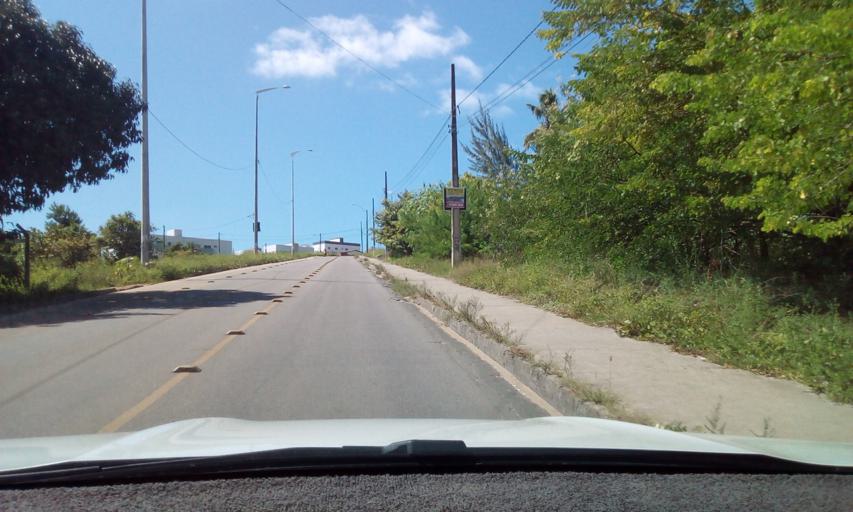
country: BR
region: Paraiba
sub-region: Joao Pessoa
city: Joao Pessoa
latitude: -7.1955
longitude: -34.8365
